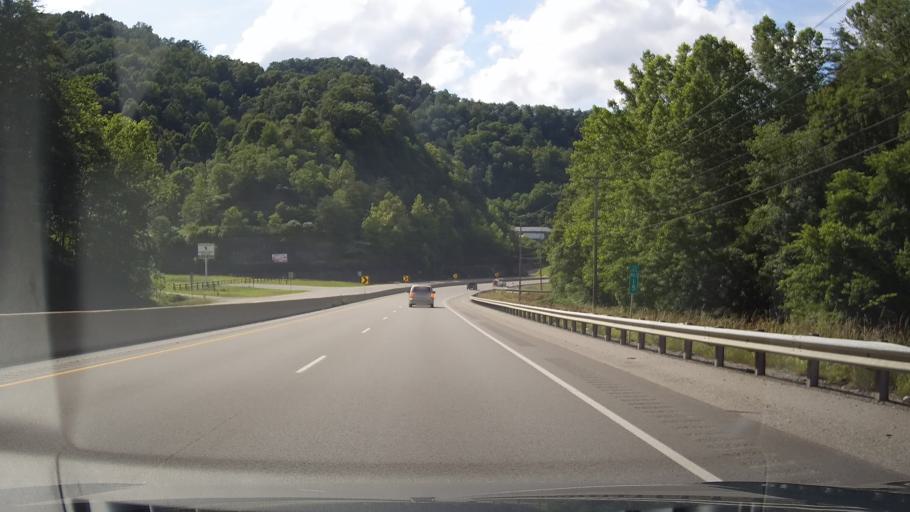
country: US
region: Kentucky
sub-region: Floyd County
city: Prestonsburg
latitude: 37.6487
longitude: -82.7827
